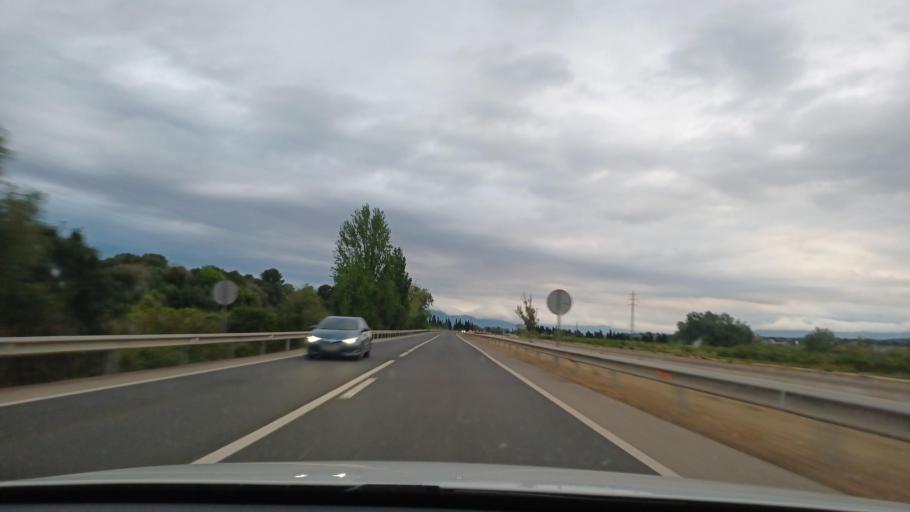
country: ES
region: Catalonia
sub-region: Provincia de Tarragona
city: Masdenverge
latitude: 40.7609
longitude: 0.5346
